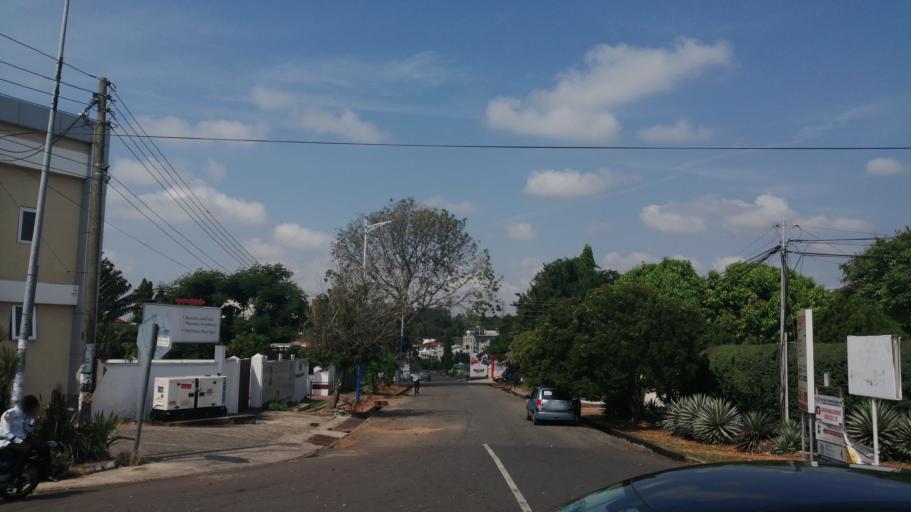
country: GH
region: Greater Accra
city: Medina Estates
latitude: 5.6345
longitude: -0.1723
